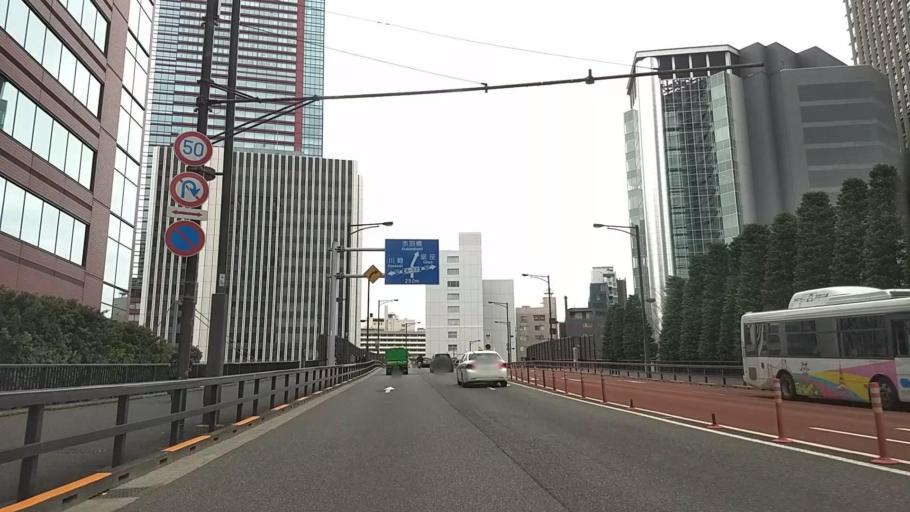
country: JP
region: Tokyo
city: Tokyo
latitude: 35.6428
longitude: 139.7454
